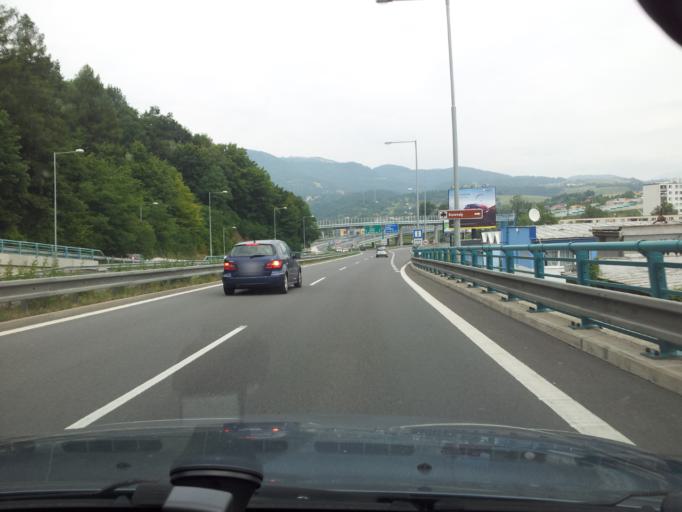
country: SK
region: Banskobystricky
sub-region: Okres Banska Bystrica
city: Banska Bystrica
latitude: 48.7463
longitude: 19.1383
